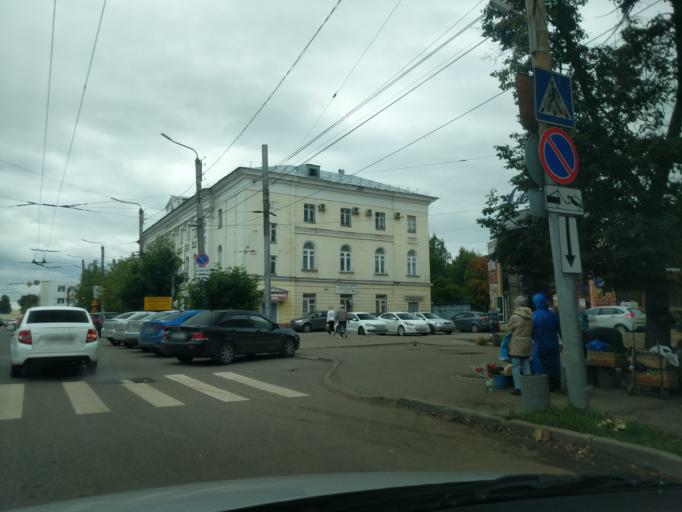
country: RU
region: Kirov
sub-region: Kirovo-Chepetskiy Rayon
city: Kirov
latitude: 58.6380
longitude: 49.6138
